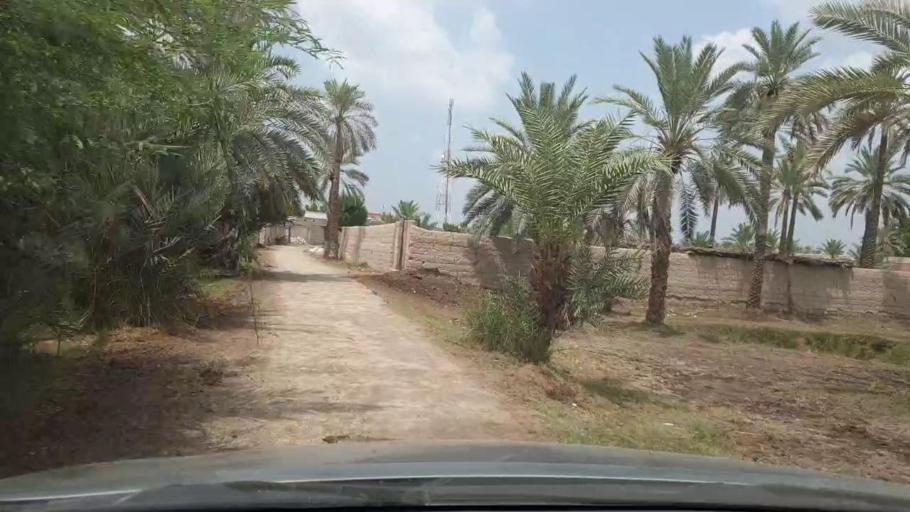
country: PK
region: Sindh
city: Khairpur
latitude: 27.4279
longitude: 68.7710
